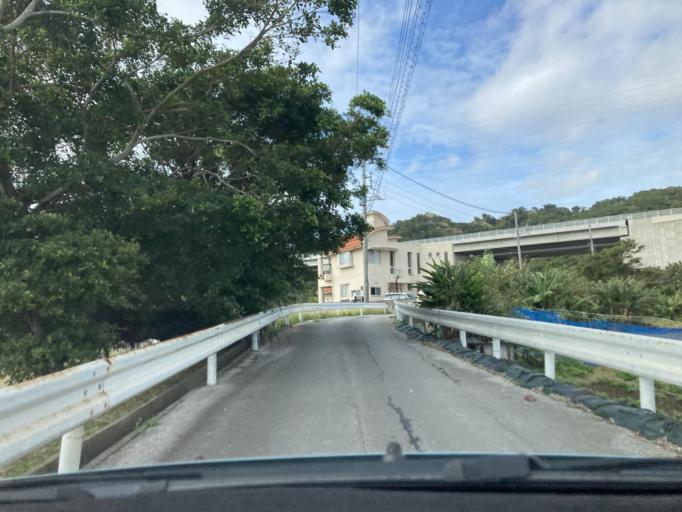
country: JP
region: Okinawa
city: Ginowan
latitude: 26.2084
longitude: 127.7543
